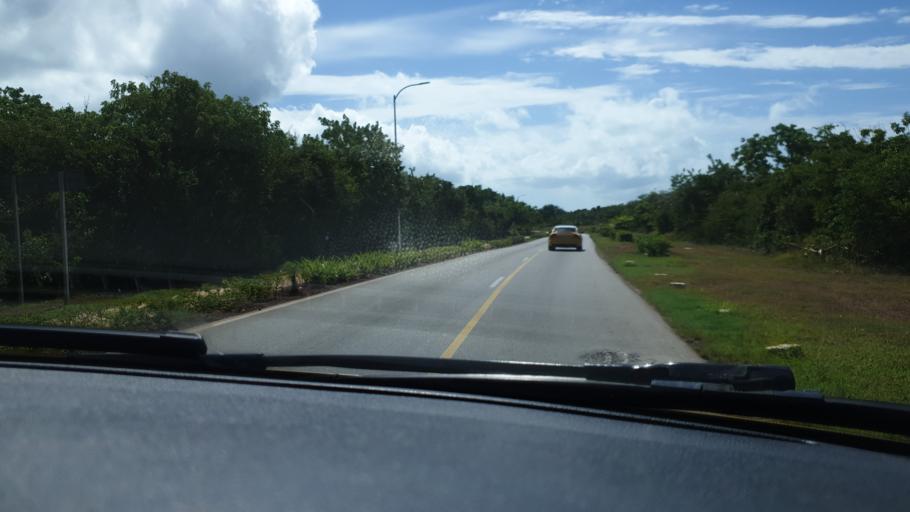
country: CU
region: Sancti Spiritus
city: Yaguajay
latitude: 22.6561
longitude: -79.0349
